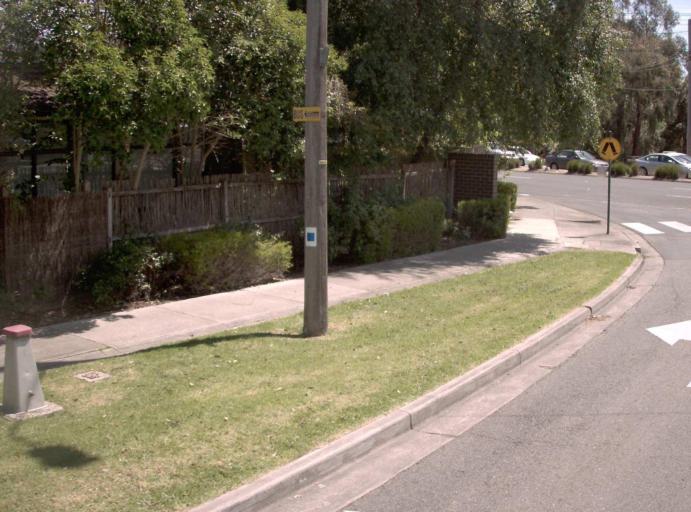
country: AU
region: Victoria
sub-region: Whitehorse
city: Blackburn South
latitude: -37.8331
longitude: 145.1564
